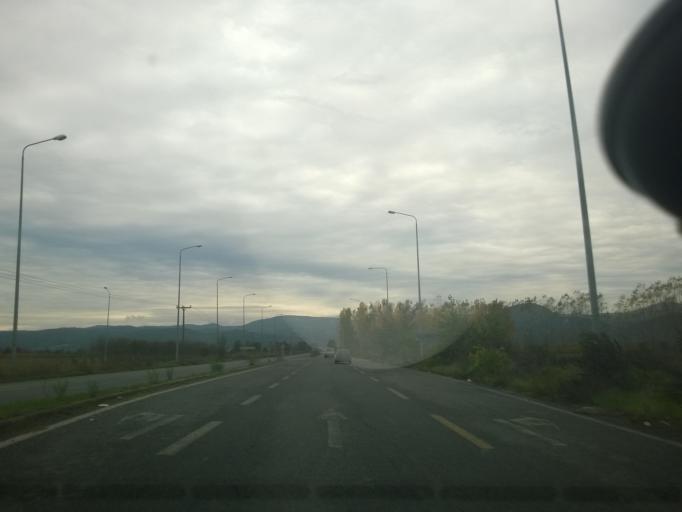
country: GR
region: Central Macedonia
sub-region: Nomos Pellis
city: Apsalos
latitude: 40.9157
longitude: 22.0753
